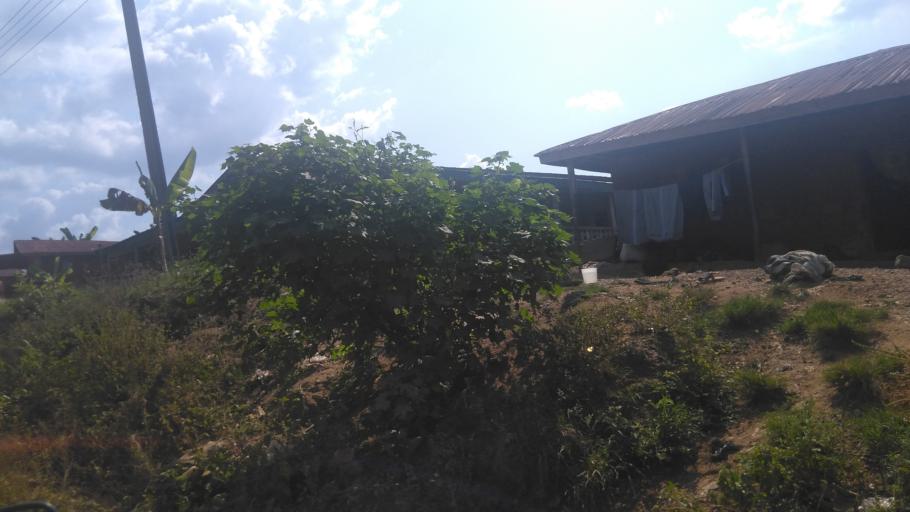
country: NG
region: Osun
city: Ifetedo
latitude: 7.0226
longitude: 4.6308
